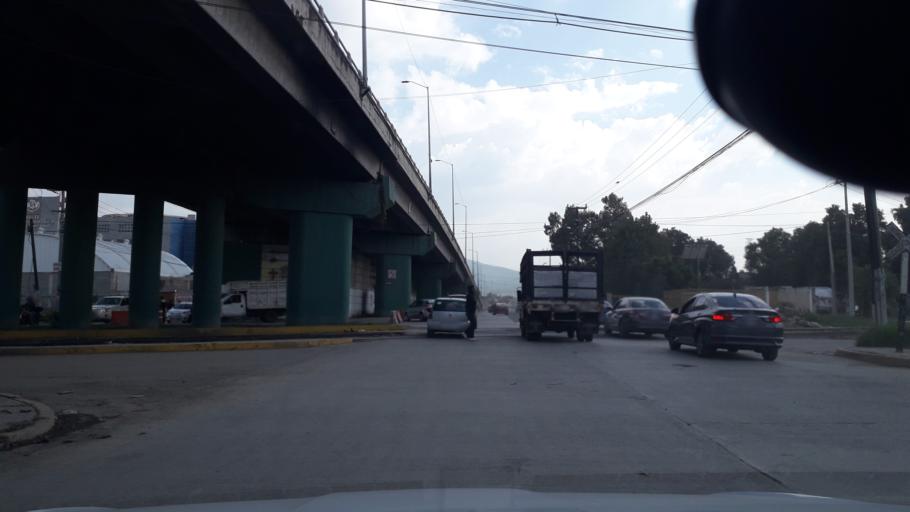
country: MX
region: Mexico
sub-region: Tultitlan
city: Colonia Lazaro Cardenas (Los Hornos)
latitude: 19.6303
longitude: -99.1651
